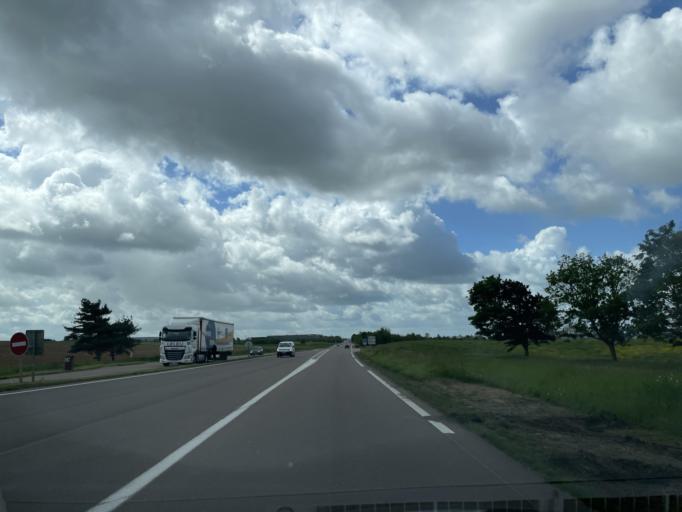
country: FR
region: Bourgogne
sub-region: Departement de l'Yonne
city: Saint-Clement
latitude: 48.2101
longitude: 3.3105
